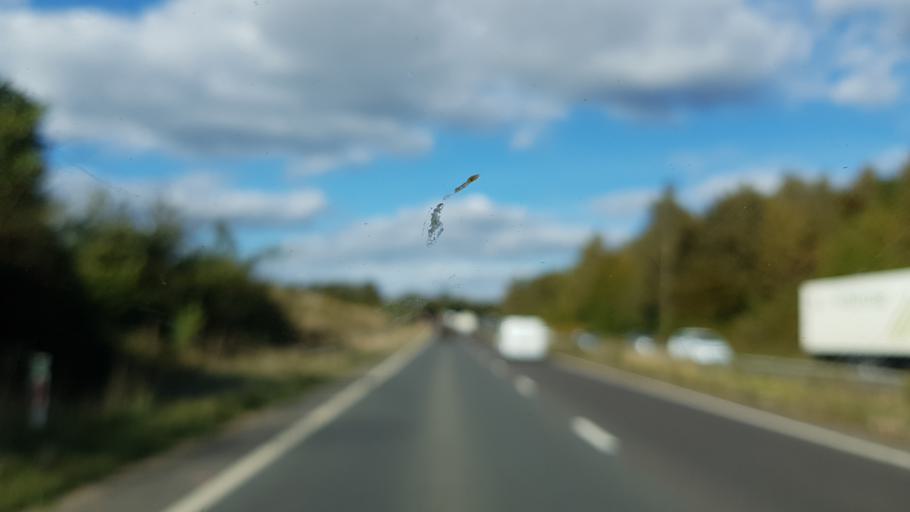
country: GB
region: England
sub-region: Surrey
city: Milford
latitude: 51.2063
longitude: -0.6509
